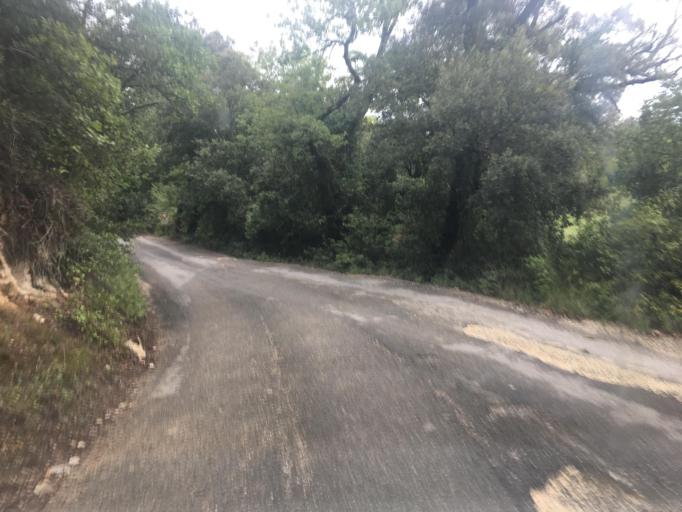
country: FR
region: Languedoc-Roussillon
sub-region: Departement du Gard
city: Montaren-et-Saint-Mediers
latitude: 43.9996
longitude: 4.3855
